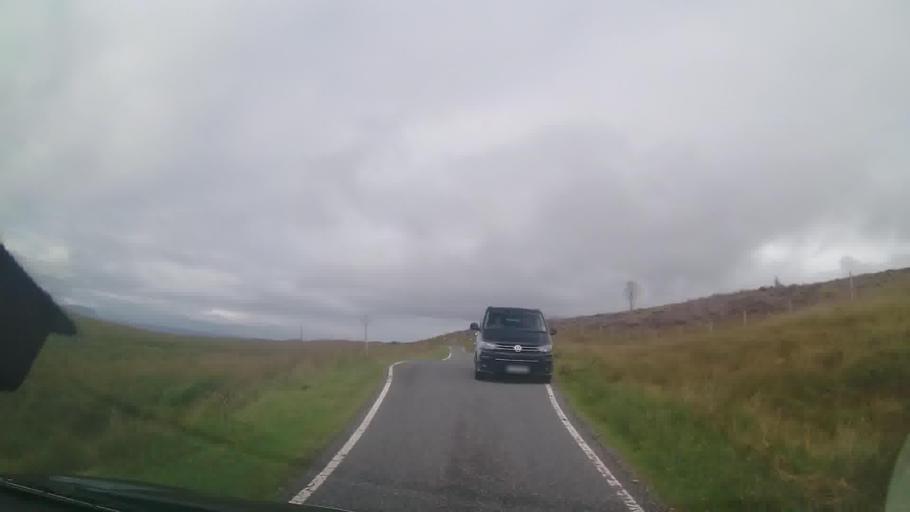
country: GB
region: Scotland
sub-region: Argyll and Bute
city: Isle Of Mull
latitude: 56.7254
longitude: -6.0384
